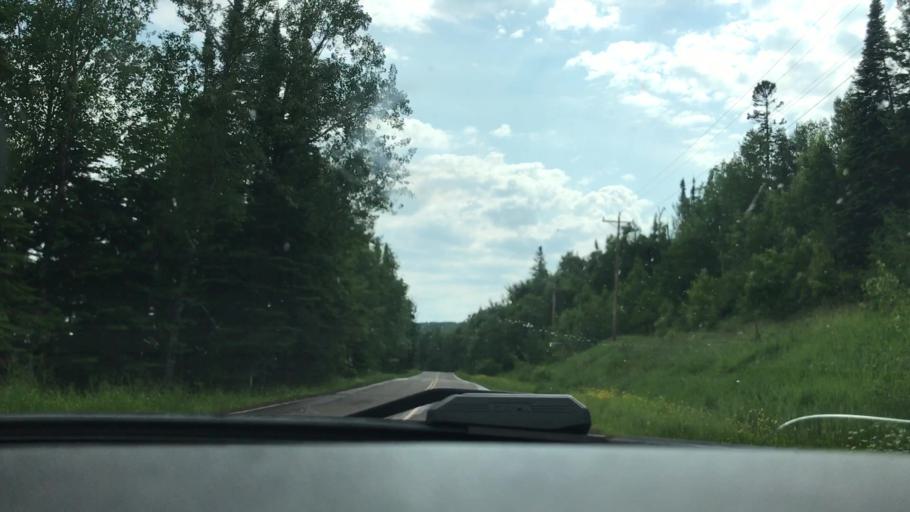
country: CA
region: Ontario
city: Neebing
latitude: 47.9573
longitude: -89.6915
